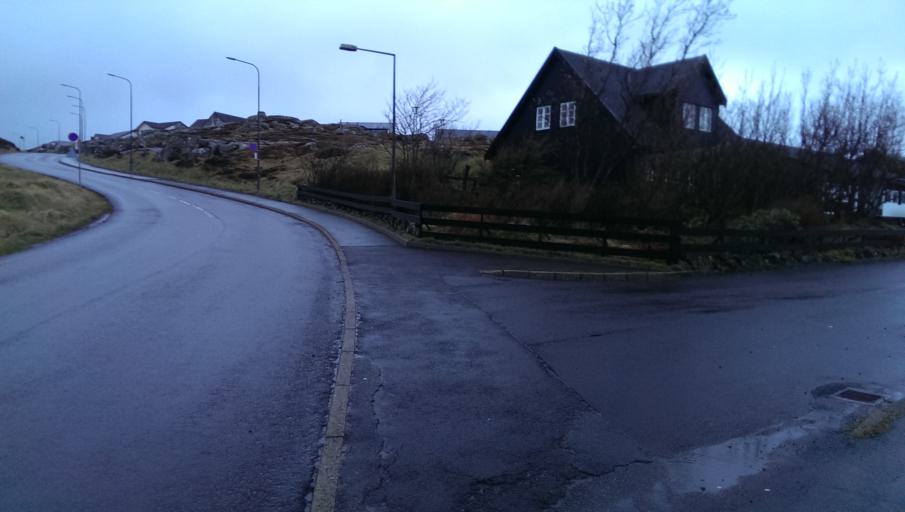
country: FO
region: Streymoy
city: Hoyvik
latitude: 62.0303
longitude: -6.7853
